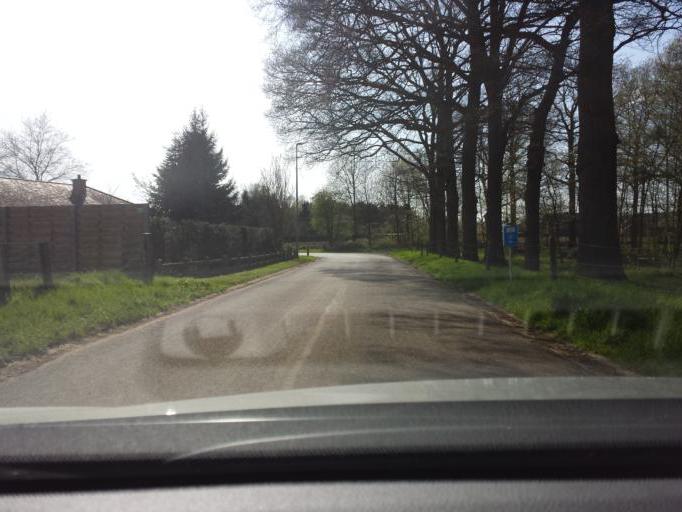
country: BE
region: Flanders
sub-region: Provincie Limburg
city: Lummen
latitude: 51.0087
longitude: 5.1488
